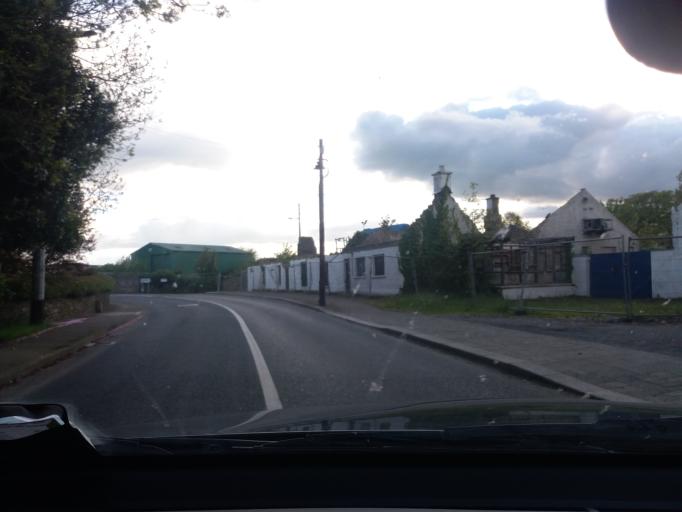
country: IE
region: Leinster
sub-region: South Dublin
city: Newcastle
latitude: 53.2996
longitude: -6.5064
